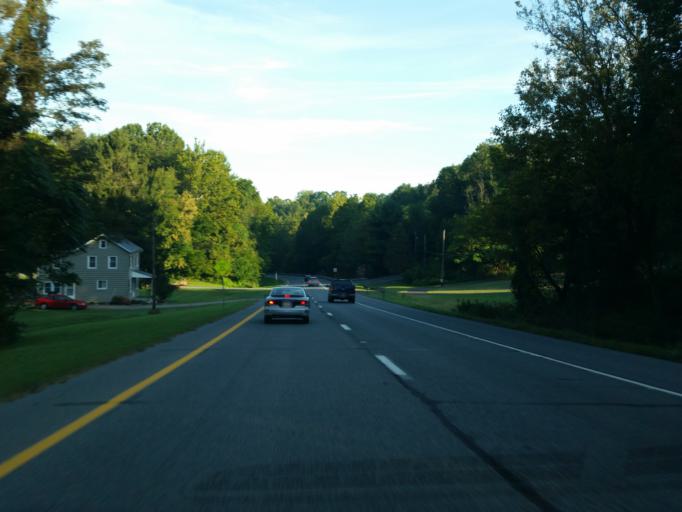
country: US
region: Pennsylvania
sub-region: Lancaster County
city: Willow Street
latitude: 39.9218
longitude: -76.2483
